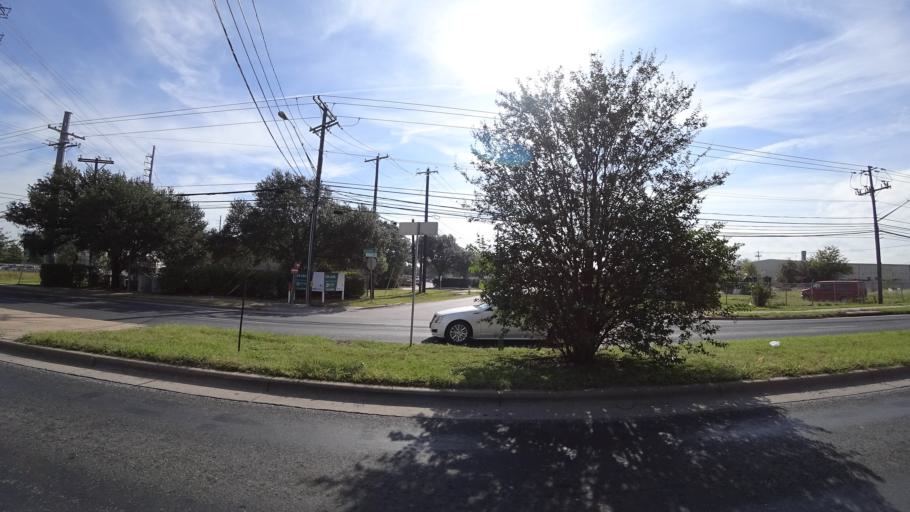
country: US
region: Texas
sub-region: Travis County
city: Austin
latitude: 30.2067
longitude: -97.7159
